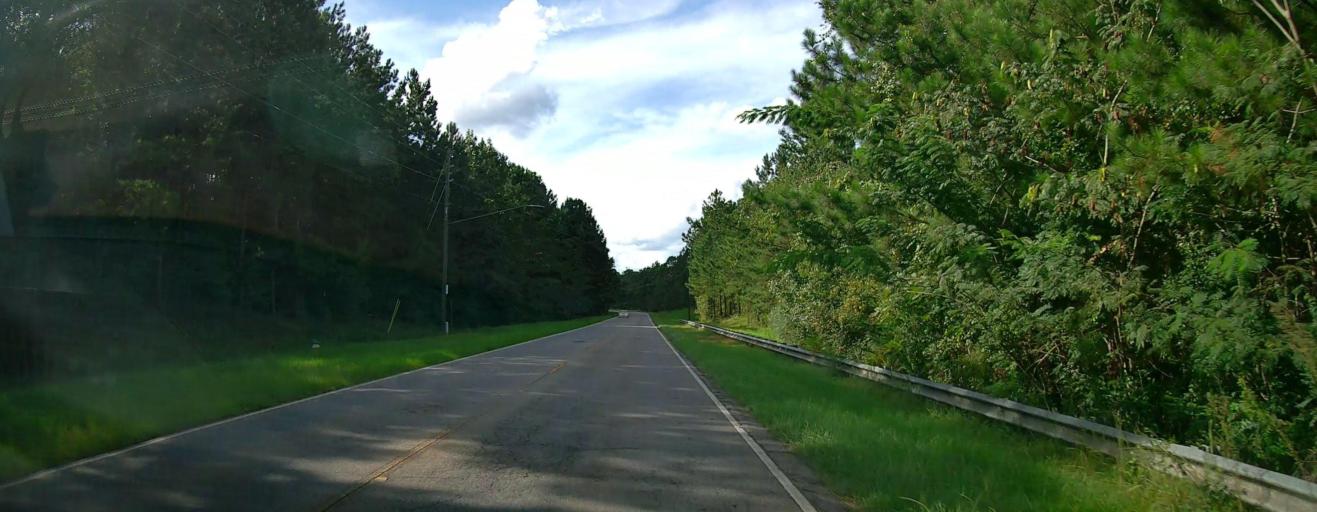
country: US
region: Alabama
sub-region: Russell County
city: Phenix City
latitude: 32.5130
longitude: -85.0096
